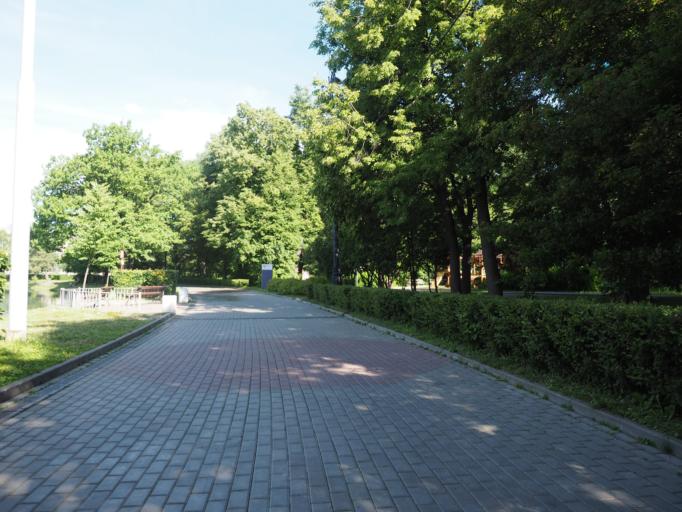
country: RU
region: Moscow
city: Ryazanskiy
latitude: 55.7729
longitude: 37.7521
